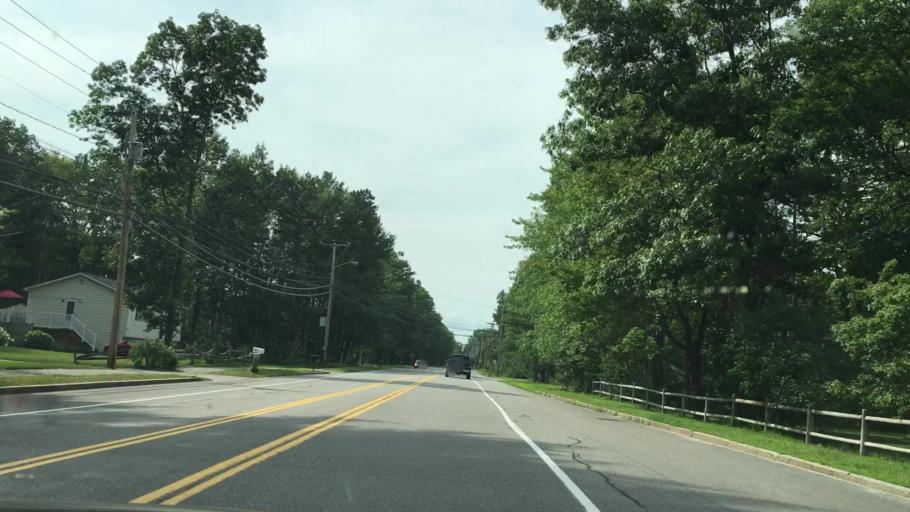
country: US
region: New Hampshire
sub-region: Merrimack County
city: East Concord
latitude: 43.2267
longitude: -71.5090
